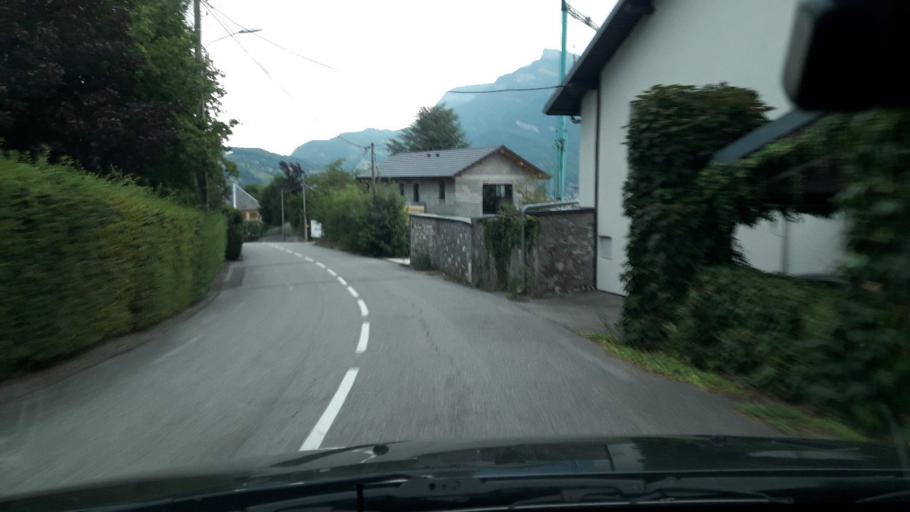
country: FR
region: Rhone-Alpes
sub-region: Departement de la Savoie
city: Barberaz
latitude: 45.5559
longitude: 5.9356
